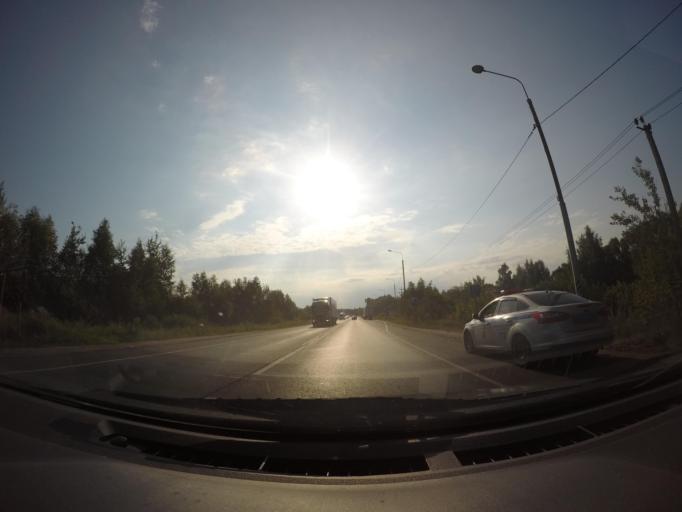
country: RU
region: Moskovskaya
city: Kratovo
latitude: 55.6403
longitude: 38.1676
